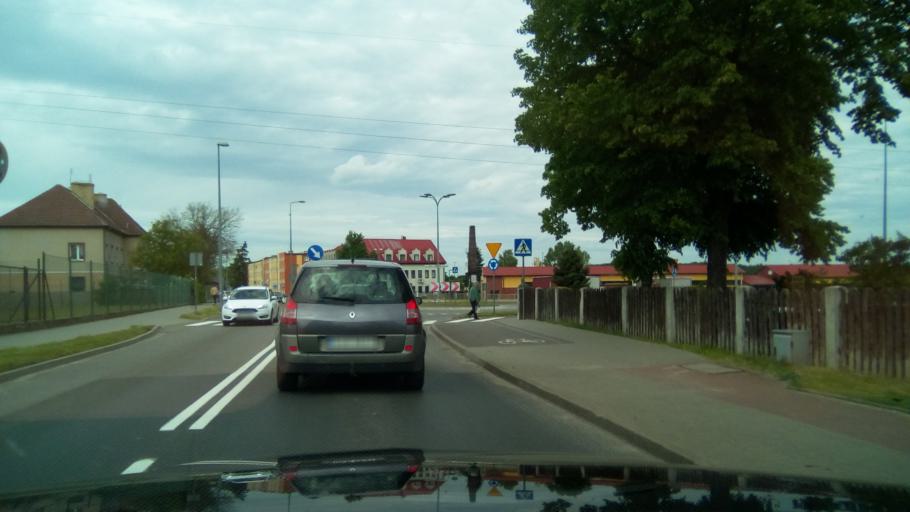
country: PL
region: Pomeranian Voivodeship
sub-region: Powiat leborski
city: Lebork
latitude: 54.5292
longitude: 17.7639
